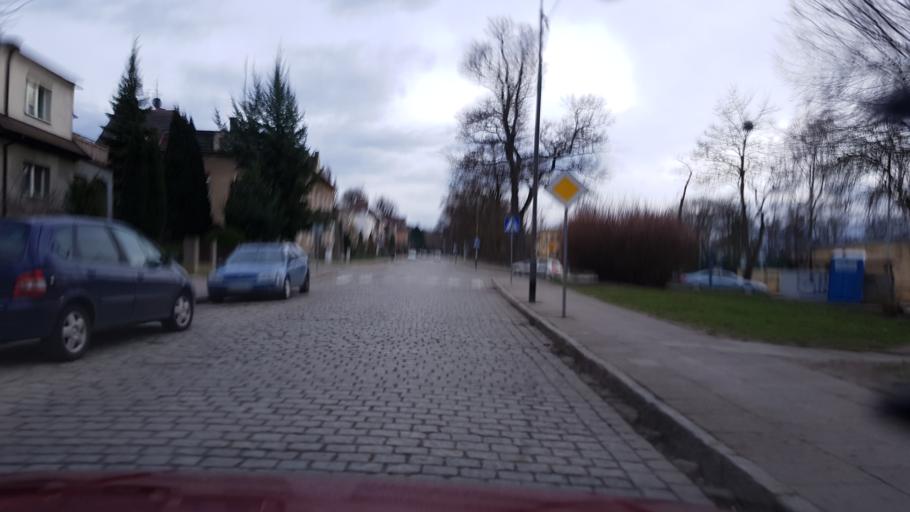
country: PL
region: West Pomeranian Voivodeship
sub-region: Szczecin
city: Szczecin
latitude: 53.3651
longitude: 14.5983
